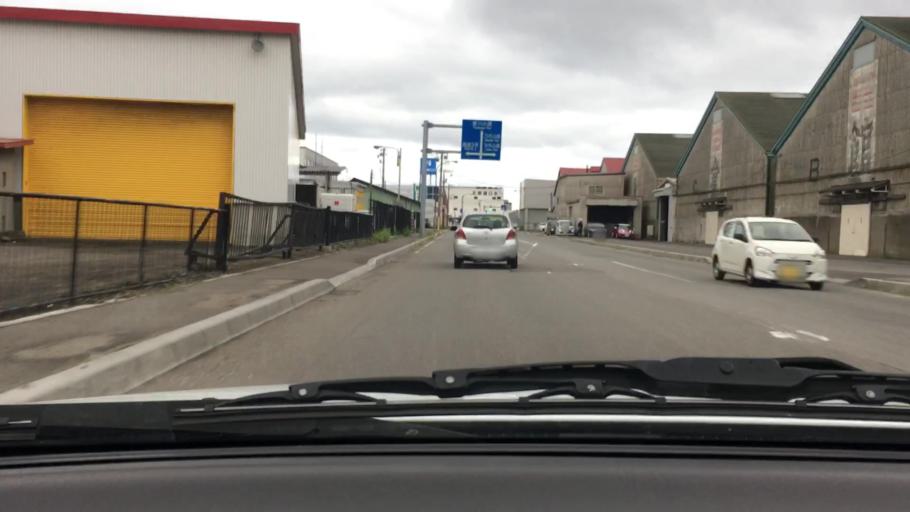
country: JP
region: Hokkaido
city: Hakodate
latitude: 41.7884
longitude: 140.7283
